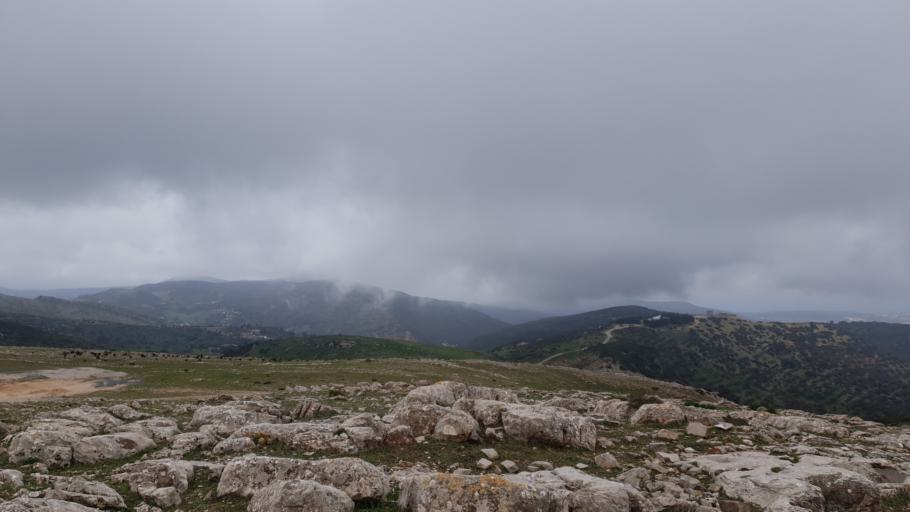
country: TN
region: Jundubah
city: Tabarka
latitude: 36.9189
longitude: 8.8822
